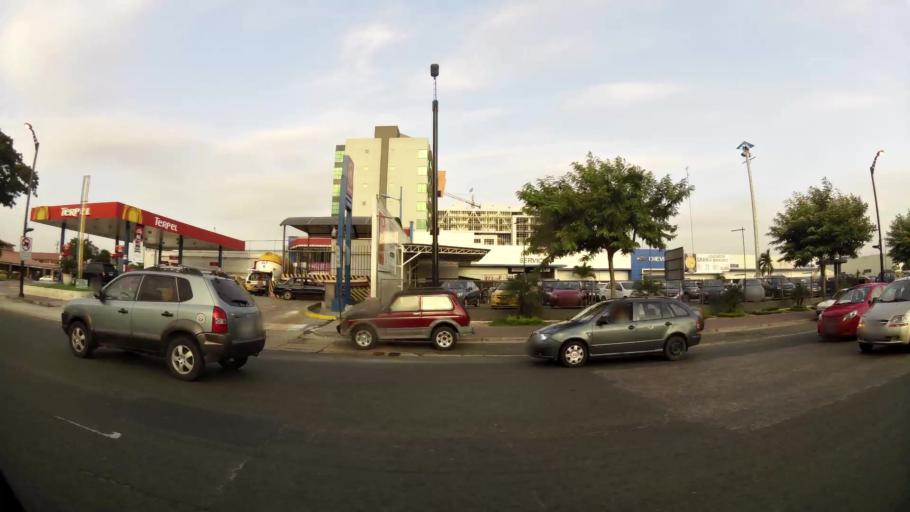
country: EC
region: Guayas
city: Eloy Alfaro
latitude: -2.1448
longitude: -79.8847
